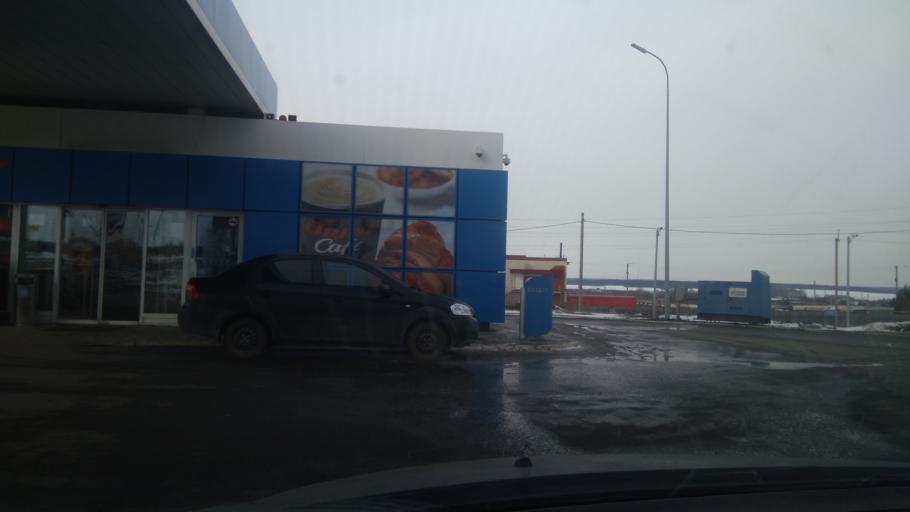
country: RU
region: Sverdlovsk
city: Achit
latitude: 56.7828
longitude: 57.9095
